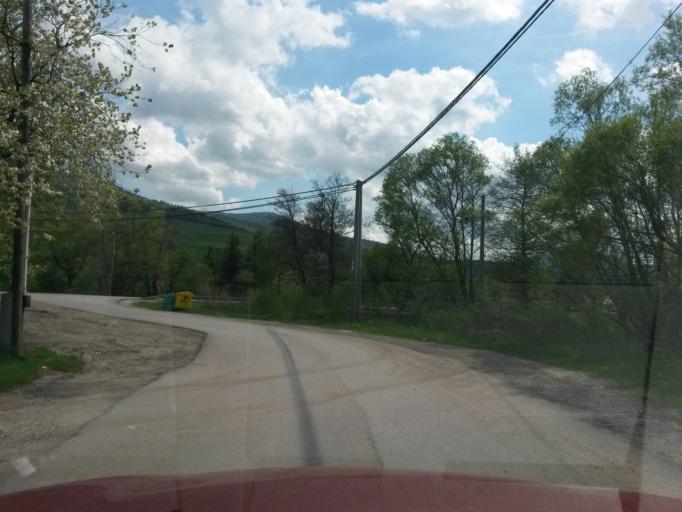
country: SK
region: Kosicky
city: Krompachy
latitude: 48.8095
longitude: 20.8095
